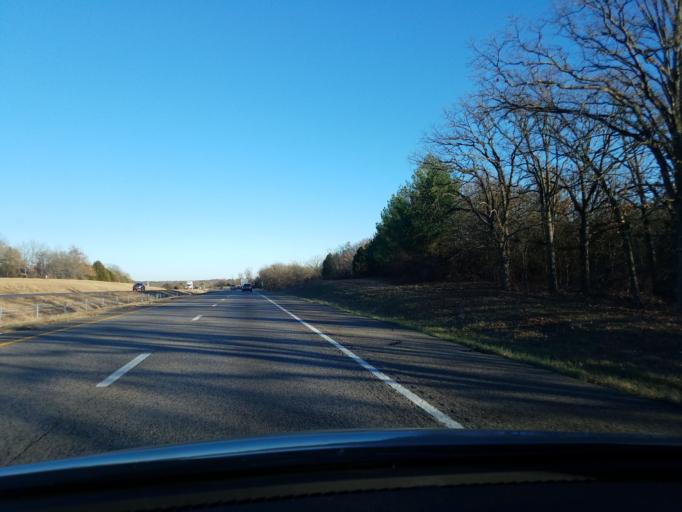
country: US
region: Missouri
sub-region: Franklin County
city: Saint Clair
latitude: 38.3027
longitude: -91.0792
